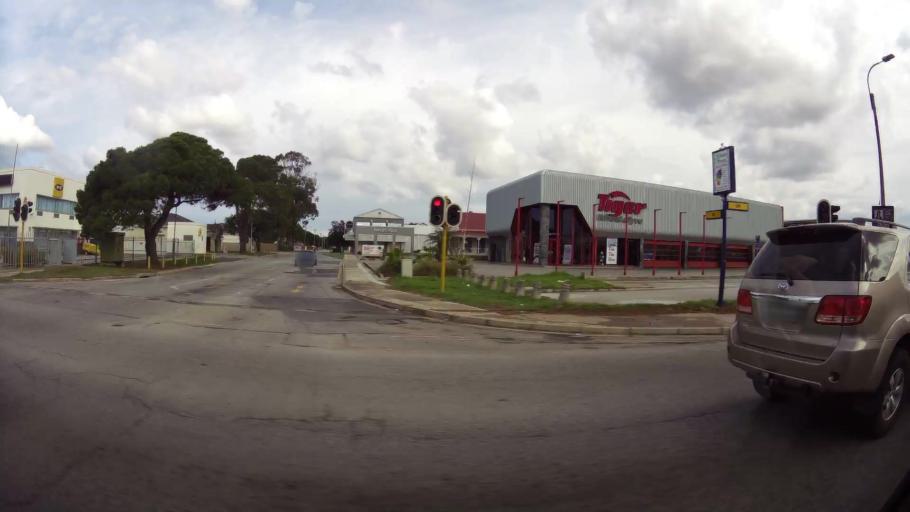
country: ZA
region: Eastern Cape
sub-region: Nelson Mandela Bay Metropolitan Municipality
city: Port Elizabeth
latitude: -33.9501
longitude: 25.5712
